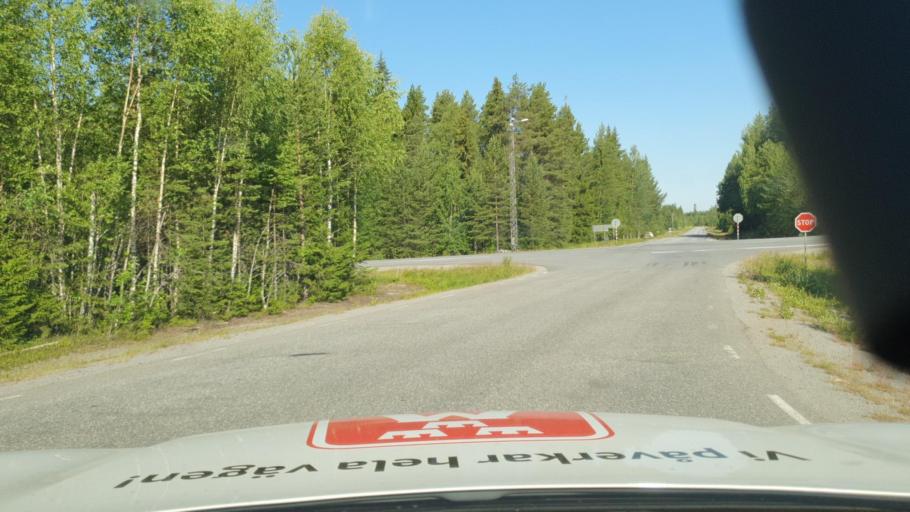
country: SE
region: Vaesterbotten
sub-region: Skelleftea Kommun
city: Ursviken
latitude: 64.6731
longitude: 21.1712
